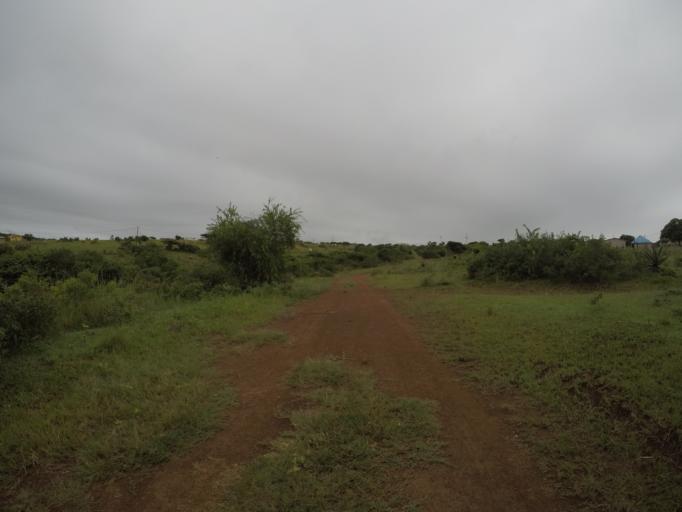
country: ZA
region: KwaZulu-Natal
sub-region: uThungulu District Municipality
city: Empangeni
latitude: -28.6064
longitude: 31.8429
